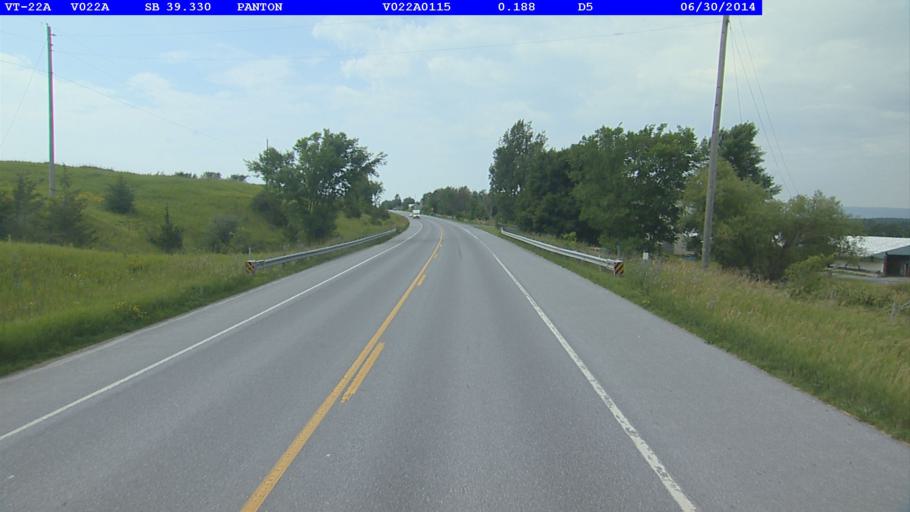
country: US
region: Vermont
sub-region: Addison County
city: Vergennes
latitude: 44.1224
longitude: -73.2932
